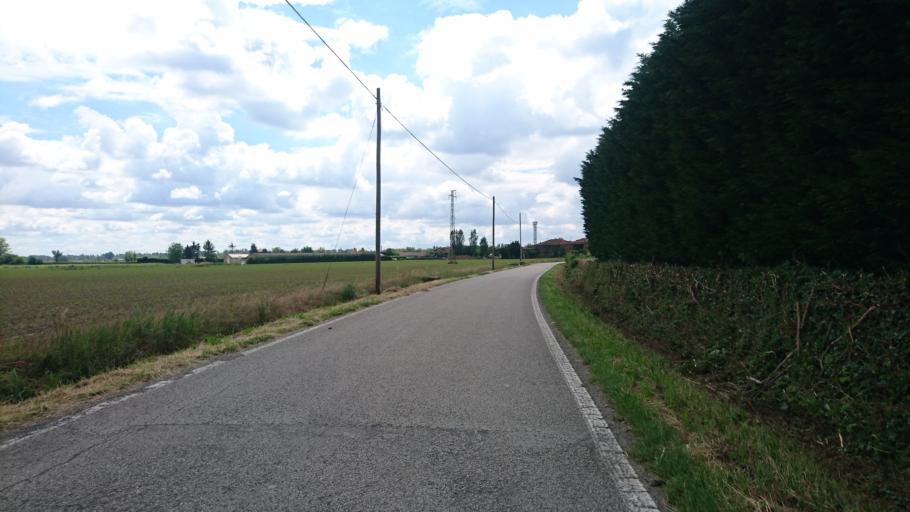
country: IT
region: Veneto
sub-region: Provincia di Padova
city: Villa Estense
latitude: 45.1524
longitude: 11.6496
